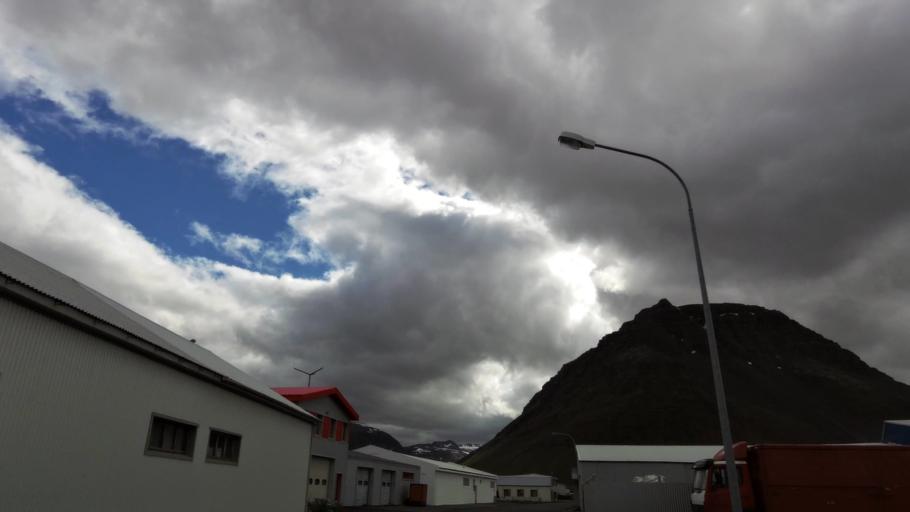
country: IS
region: Westfjords
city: Isafjoerdur
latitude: 66.1585
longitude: -23.2470
